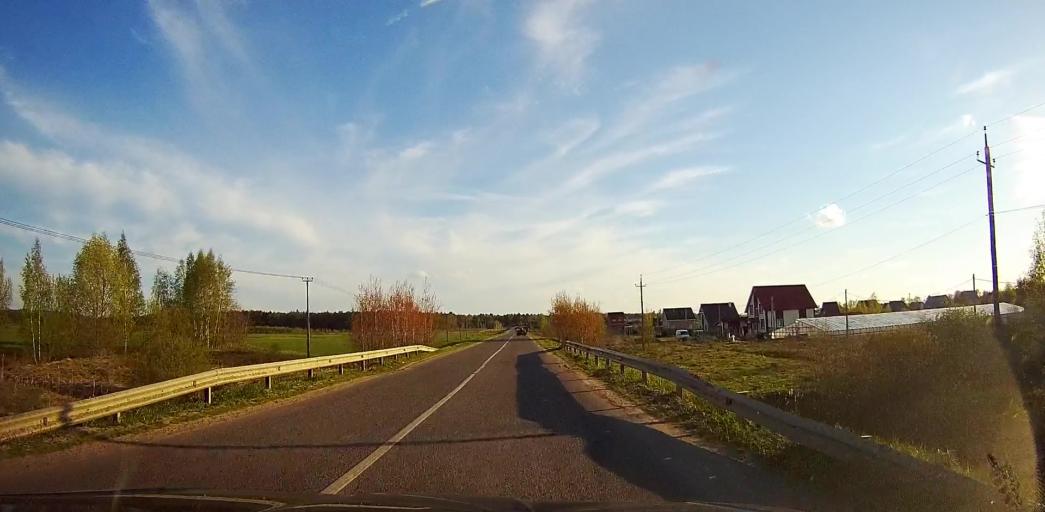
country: RU
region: Moskovskaya
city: Bronnitsy
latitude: 55.2817
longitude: 38.1727
